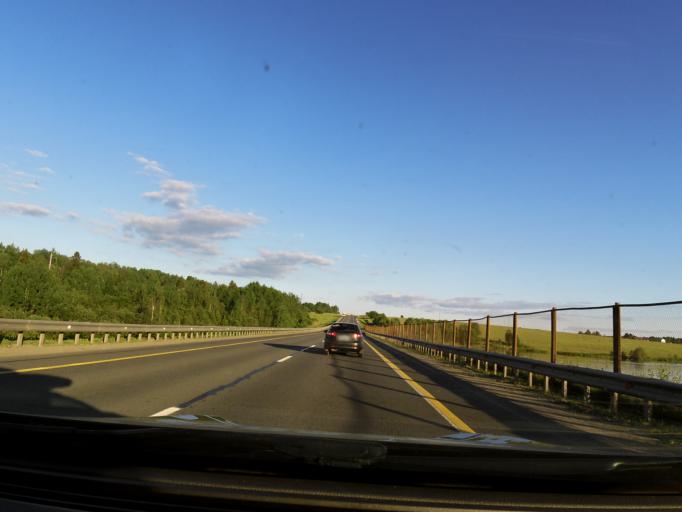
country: RU
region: Vologda
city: Vologda
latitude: 59.1173
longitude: 39.9736
